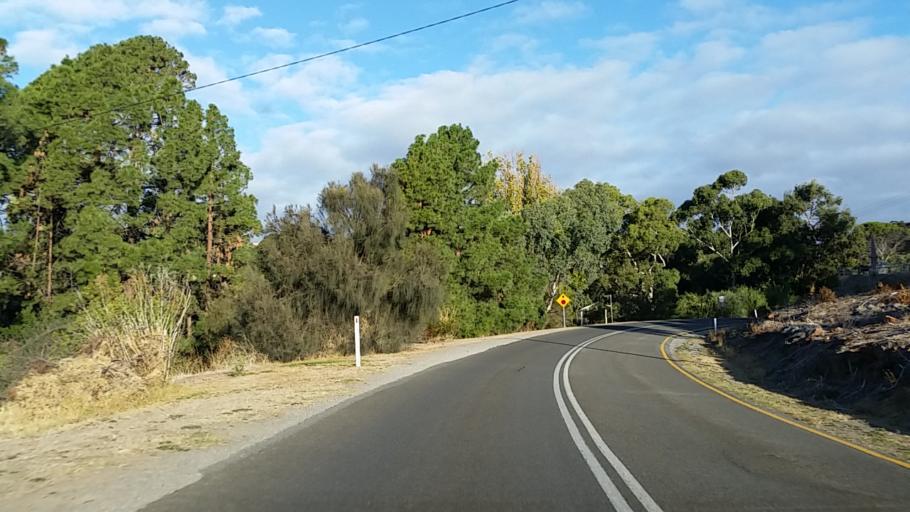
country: AU
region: South Australia
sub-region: Yankalilla
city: Normanville
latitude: -35.5263
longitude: 138.2273
